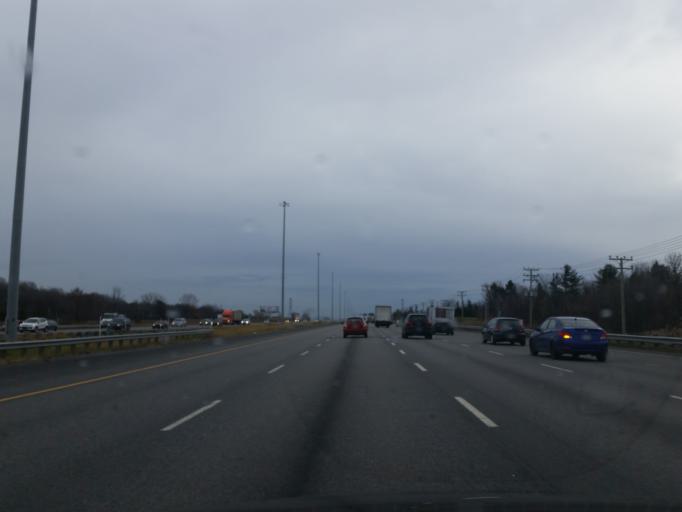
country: CA
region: Quebec
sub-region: Laurentides
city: Blainville
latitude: 45.6528
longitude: -73.8779
